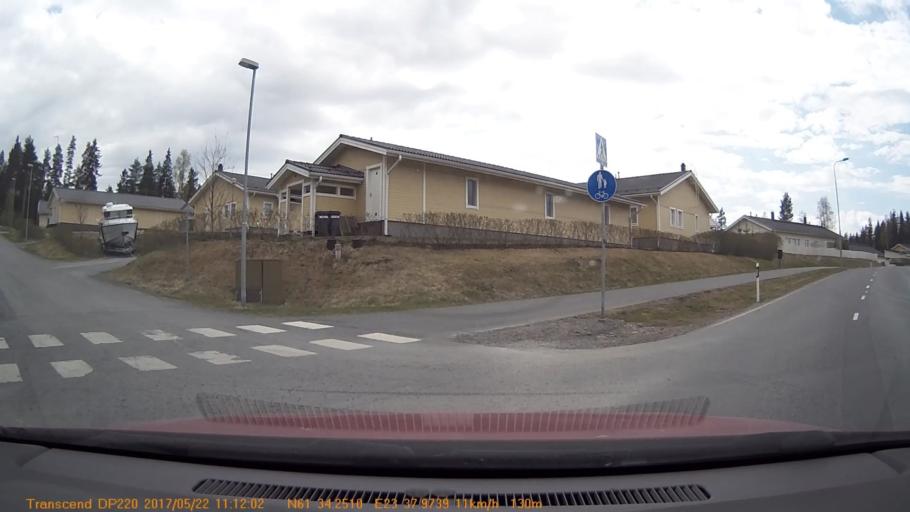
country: FI
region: Pirkanmaa
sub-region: Tampere
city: Yloejaervi
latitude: 61.5712
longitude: 23.6323
